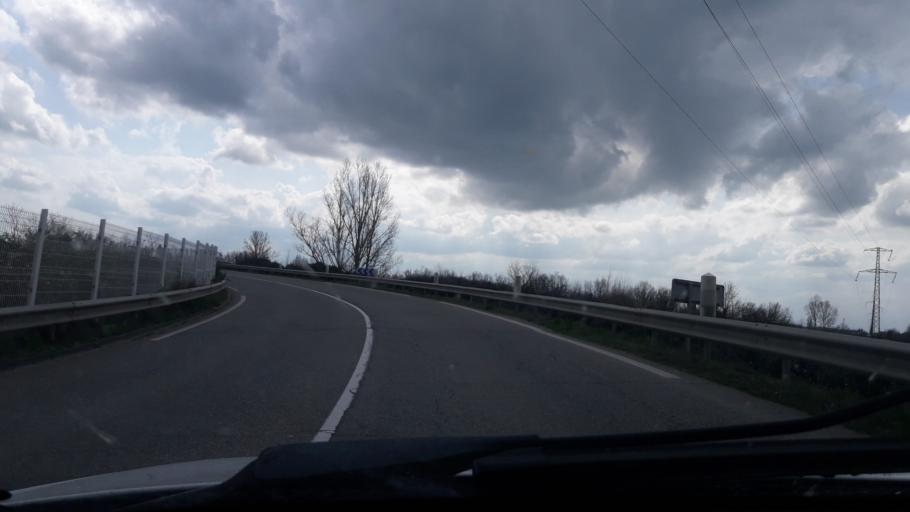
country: FR
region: Midi-Pyrenees
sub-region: Departement de la Haute-Garonne
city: Carbonne
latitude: 43.3212
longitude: 1.2163
